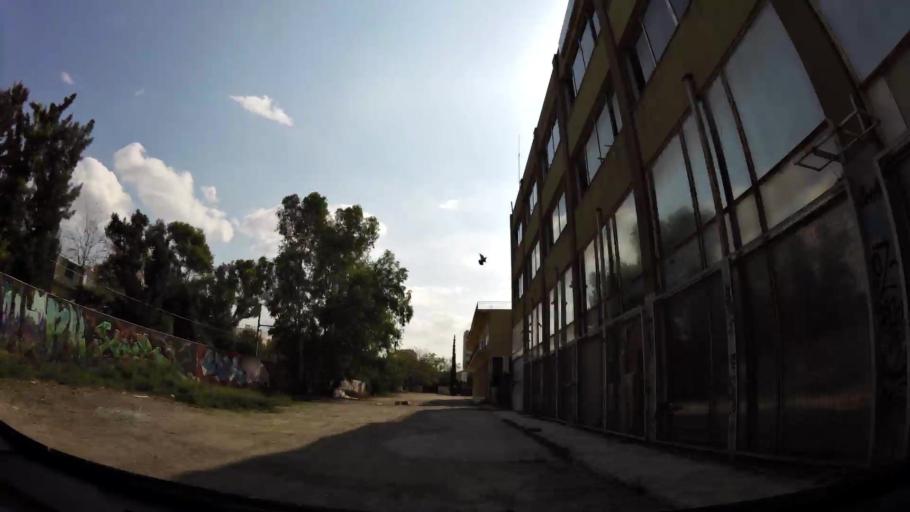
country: GR
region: Attica
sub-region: Nomarchia Athinas
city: Nea Chalkidona
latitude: 38.0116
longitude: 23.7198
